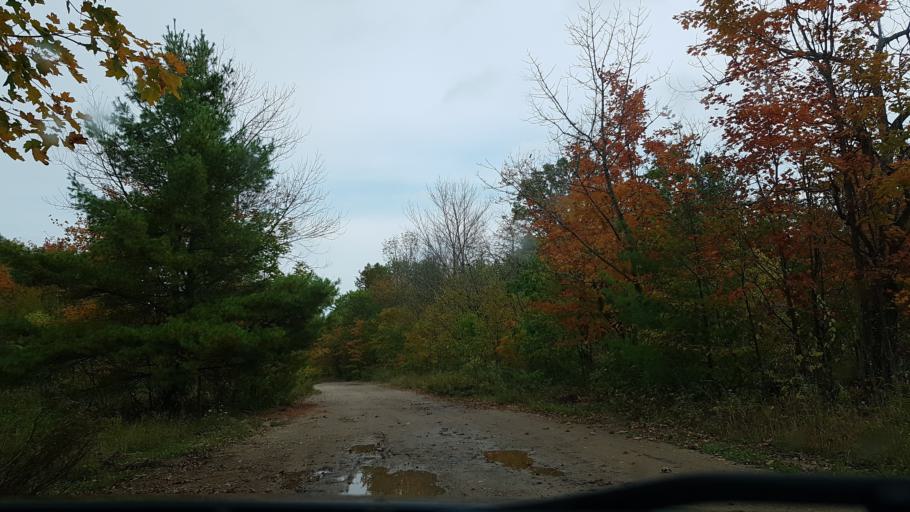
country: CA
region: Ontario
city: Gravenhurst
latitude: 44.6995
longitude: -78.9920
